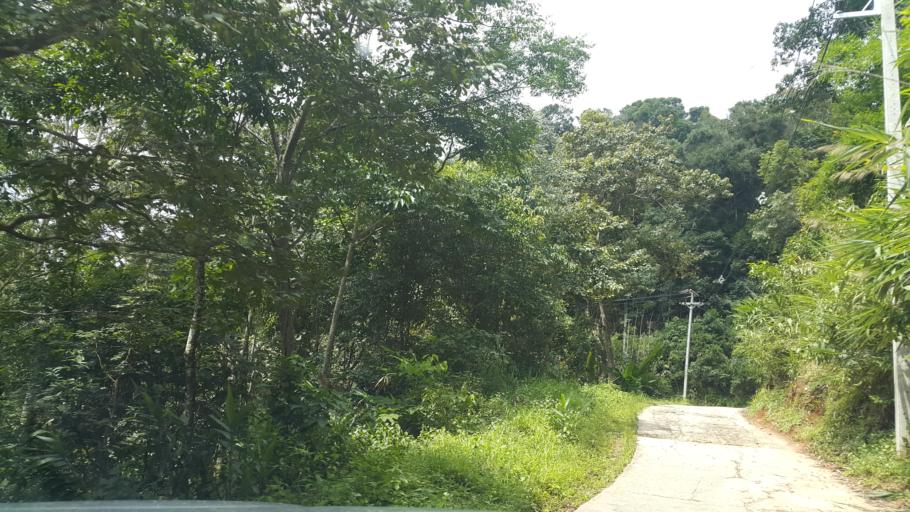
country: TH
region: Lampang
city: Wang Nuea
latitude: 19.0954
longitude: 99.3686
